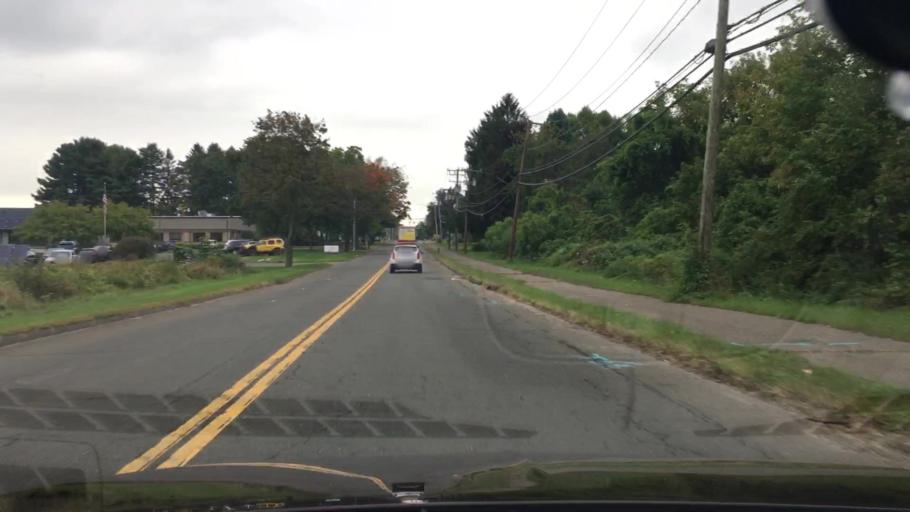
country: US
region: Connecticut
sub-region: Hartford County
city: Kensington
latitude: 41.5909
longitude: -72.7212
